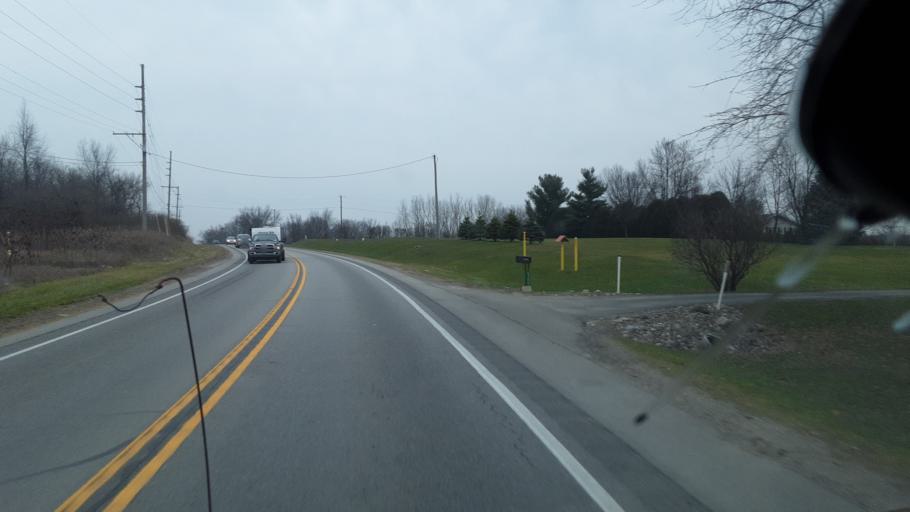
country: US
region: Indiana
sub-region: Elkhart County
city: Middlebury
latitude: 41.7160
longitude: -85.6858
